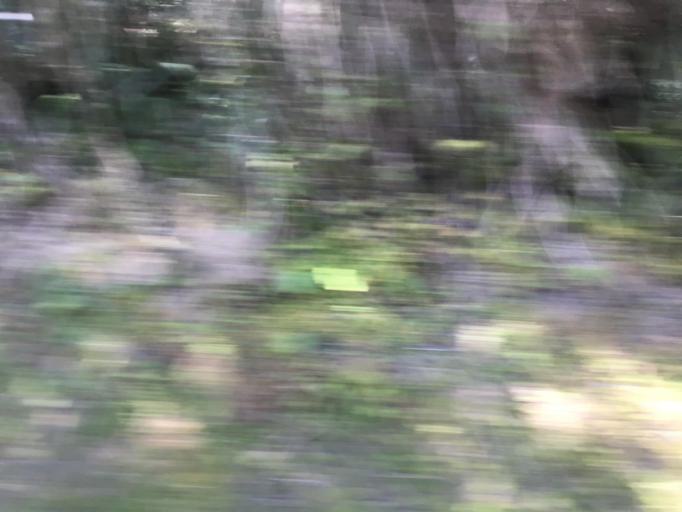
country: TW
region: Taiwan
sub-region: Yilan
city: Yilan
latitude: 24.5294
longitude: 121.5197
